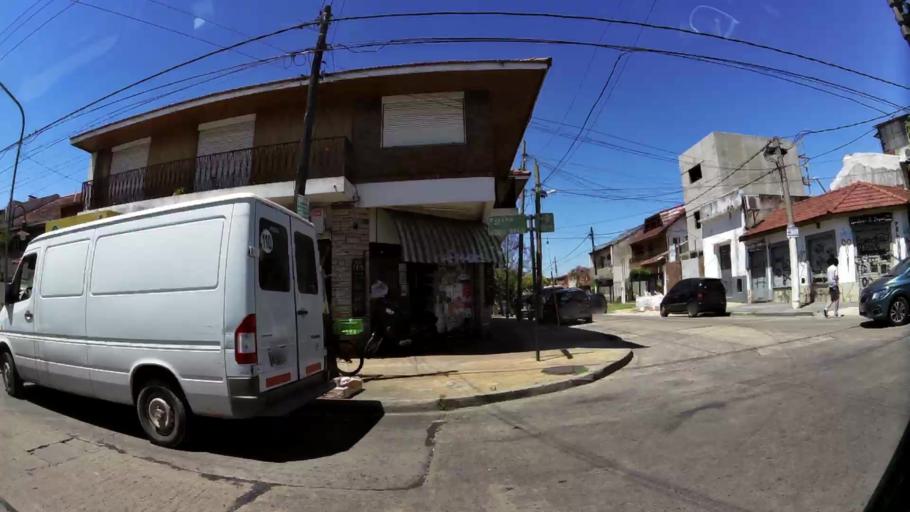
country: AR
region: Buenos Aires
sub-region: Partido de Vicente Lopez
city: Olivos
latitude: -34.5021
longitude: -58.5072
